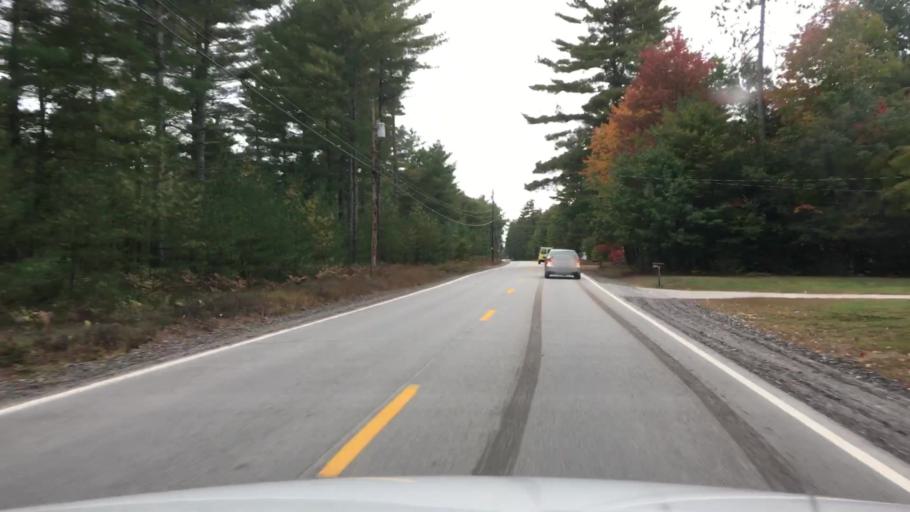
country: US
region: Maine
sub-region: Cumberland County
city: Harrison
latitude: 44.2174
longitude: -70.6872
